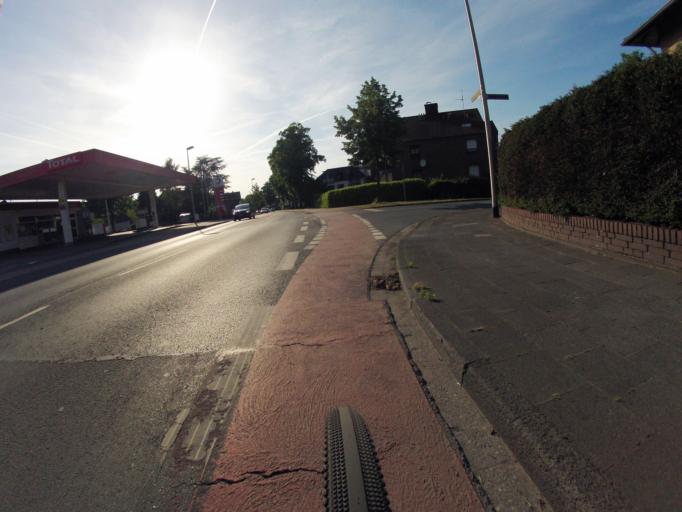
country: DE
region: North Rhine-Westphalia
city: Ibbenburen
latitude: 52.2746
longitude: 7.7052
